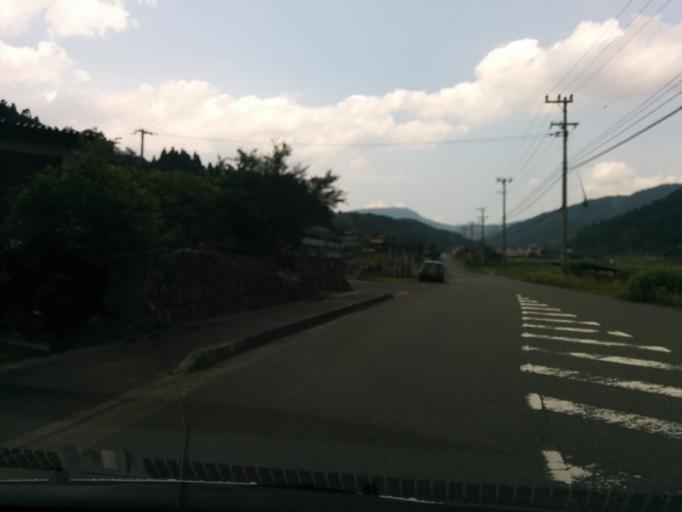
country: JP
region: Kyoto
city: Fukuchiyama
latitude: 35.4051
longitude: 135.1502
